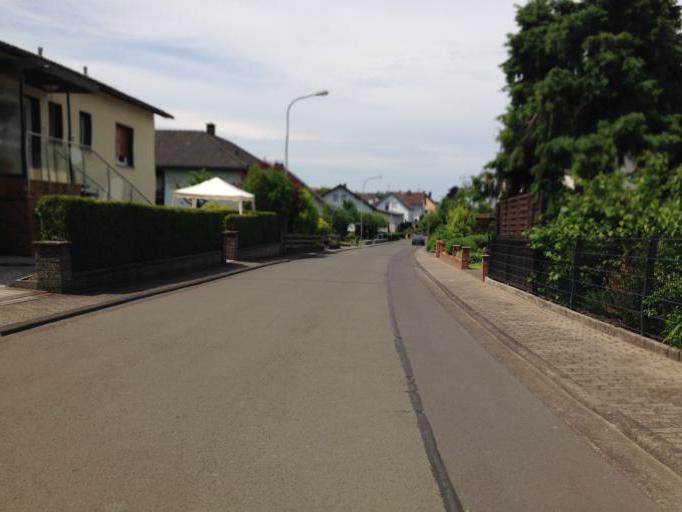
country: DE
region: Hesse
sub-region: Regierungsbezirk Giessen
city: Grossen Buseck
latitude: 50.6041
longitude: 8.7870
